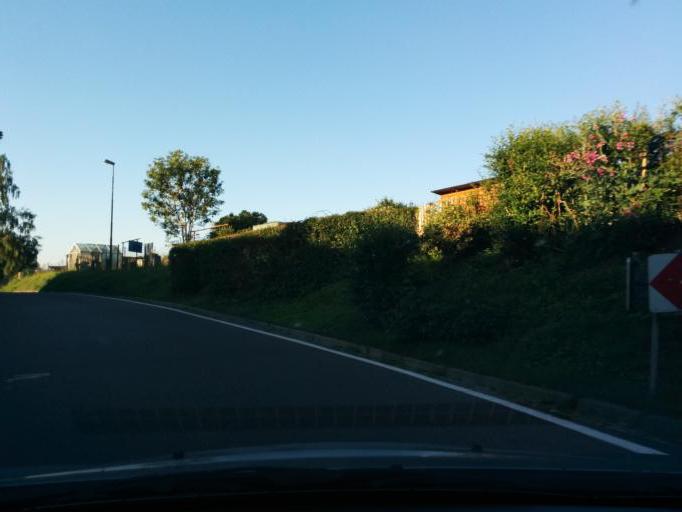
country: DE
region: Saxony
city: Floha
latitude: 50.8455
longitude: 13.0775
